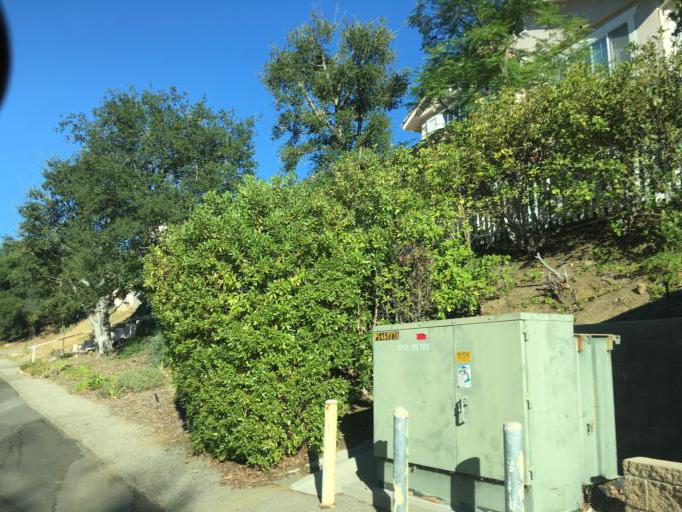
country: US
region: California
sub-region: Los Angeles County
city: Westlake Village
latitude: 34.0929
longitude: -118.8067
